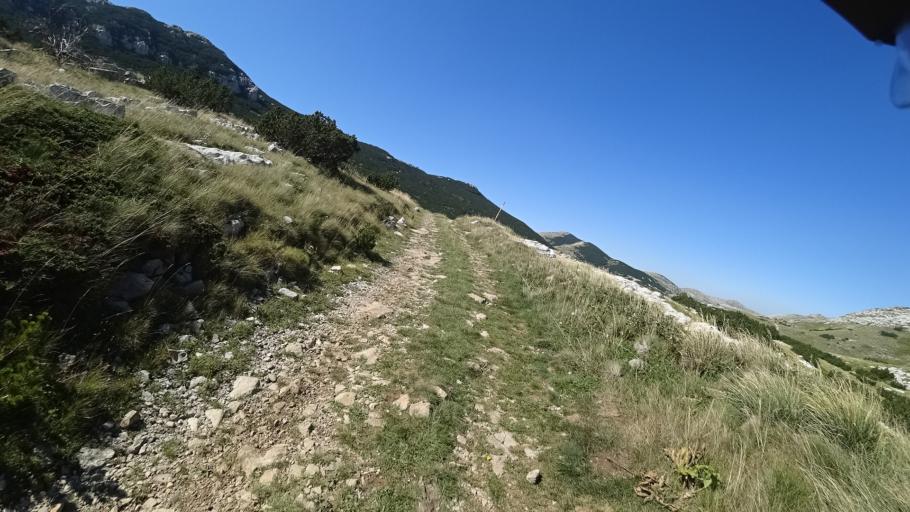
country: HR
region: Splitsko-Dalmatinska
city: Hrvace
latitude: 43.9375
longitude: 16.5910
